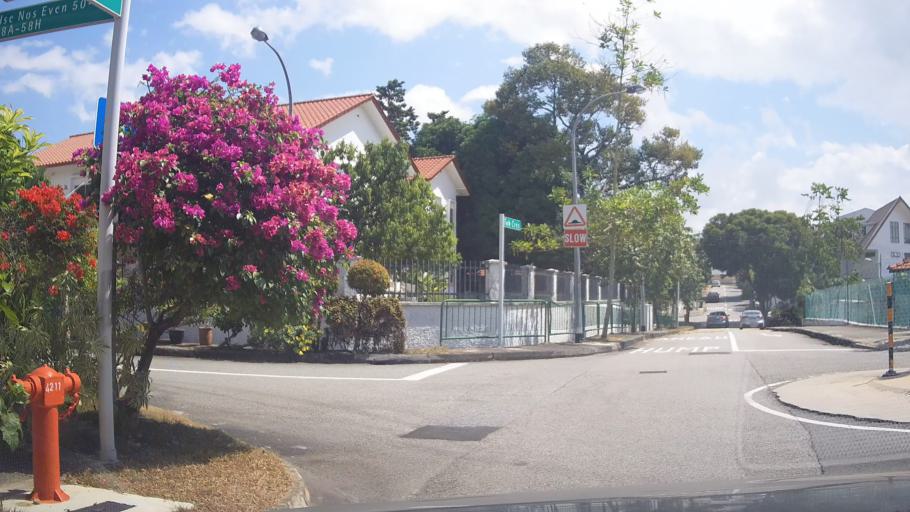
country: MY
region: Johor
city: Kampung Pasir Gudang Baru
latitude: 1.3652
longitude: 103.9711
